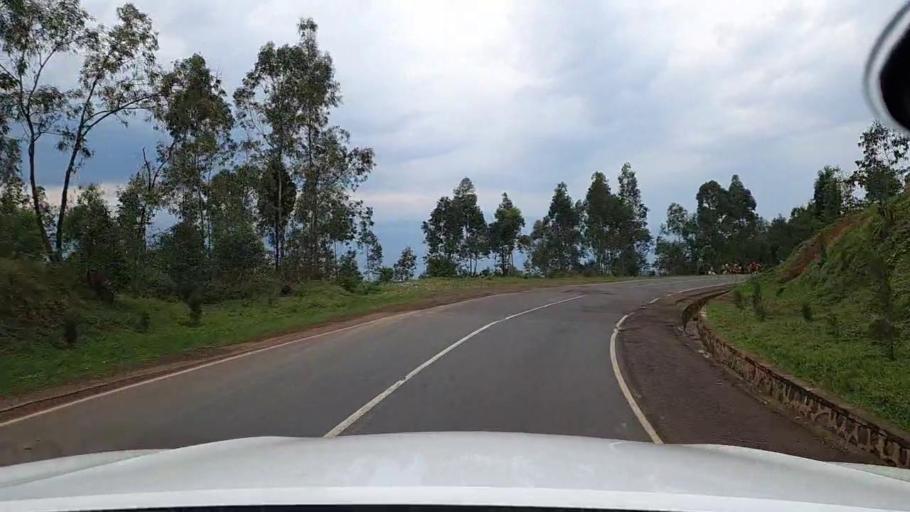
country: RW
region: Western Province
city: Cyangugu
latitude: -2.6478
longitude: 28.9655
